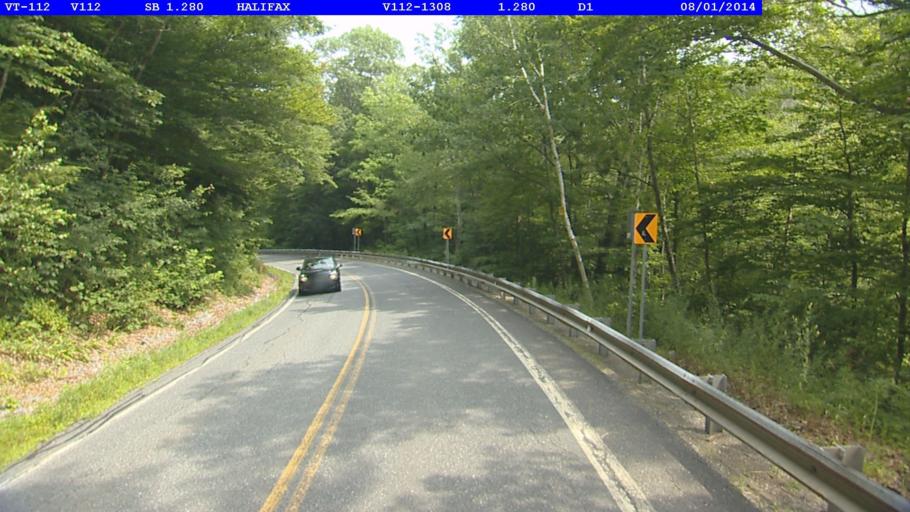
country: US
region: Massachusetts
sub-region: Franklin County
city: Colrain
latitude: 42.7452
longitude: -72.7404
